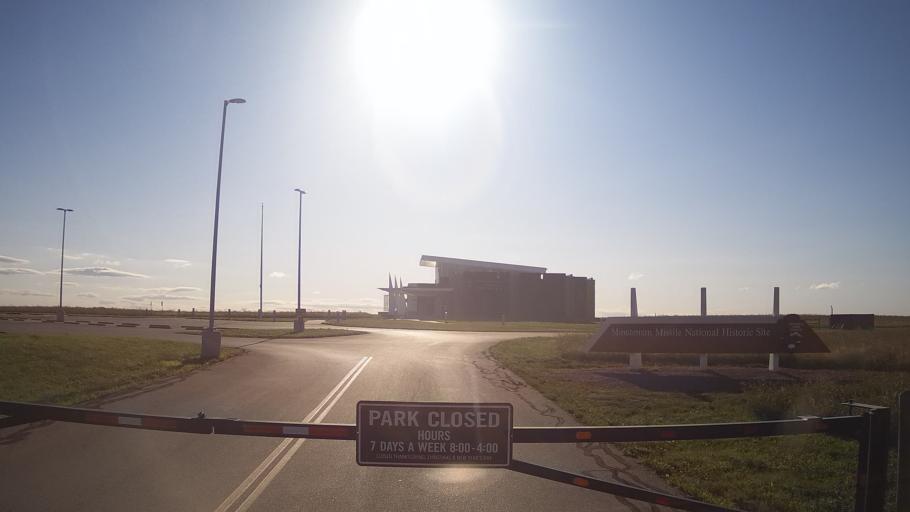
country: US
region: South Dakota
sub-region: Haakon County
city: Philip
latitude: 43.8444
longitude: -101.8998
